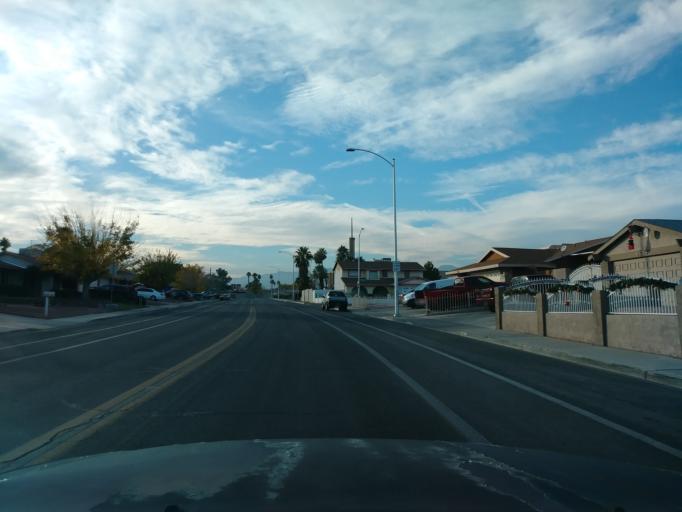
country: US
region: Nevada
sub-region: Clark County
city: Spring Valley
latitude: 36.1701
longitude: -115.2393
